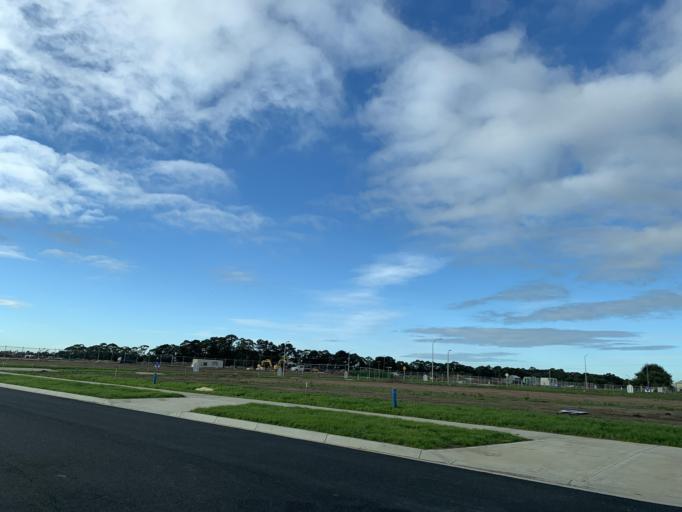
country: AU
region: Victoria
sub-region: Cardinia
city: Officer South
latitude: -38.1367
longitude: 145.3658
